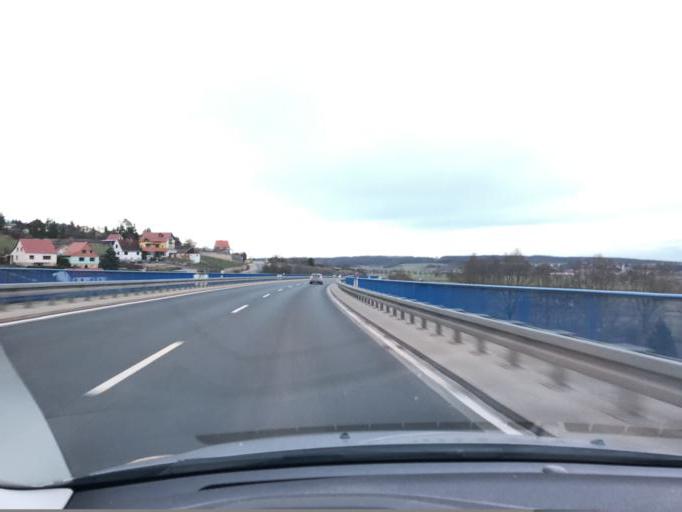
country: DE
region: Saxony-Anhalt
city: Freyburg
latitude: 51.2024
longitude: 11.7733
